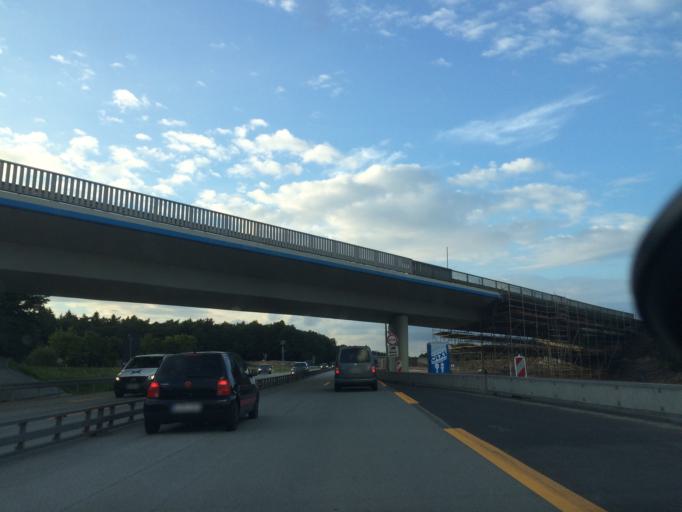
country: DE
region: Schleswig-Holstein
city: Grossenaspe
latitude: 54.0018
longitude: 9.9340
